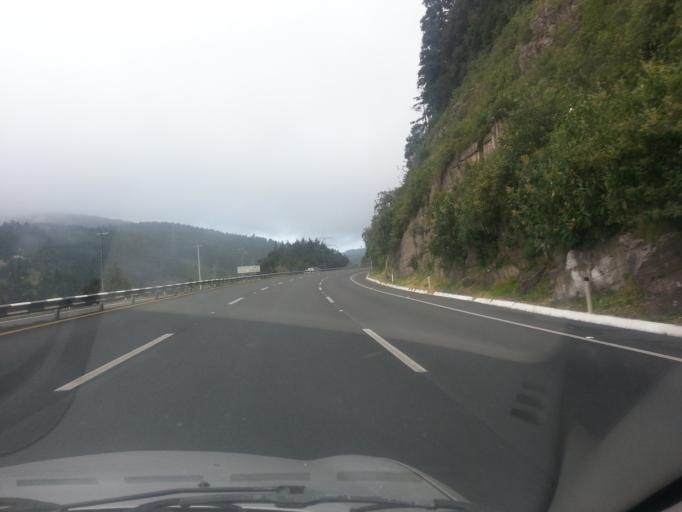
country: MX
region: Mexico City
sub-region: Cuajimalpa de Morelos
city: San Lorenzo Acopilco
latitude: 19.3125
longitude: -99.3400
